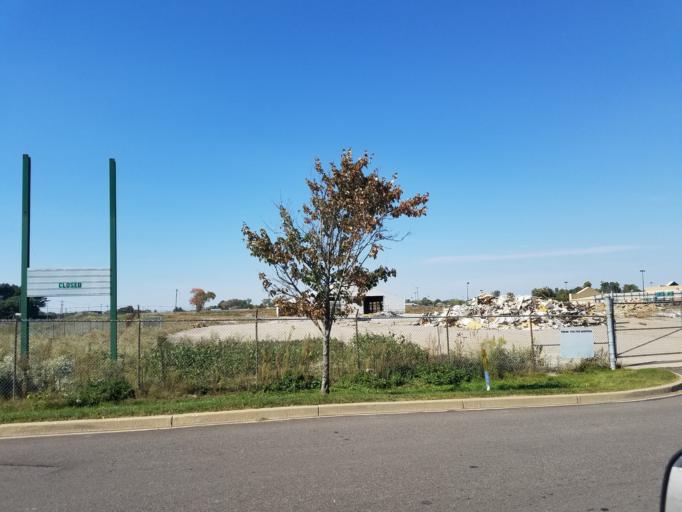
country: US
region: Ohio
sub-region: Ashland County
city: Ashland
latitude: 40.8596
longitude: -82.2693
